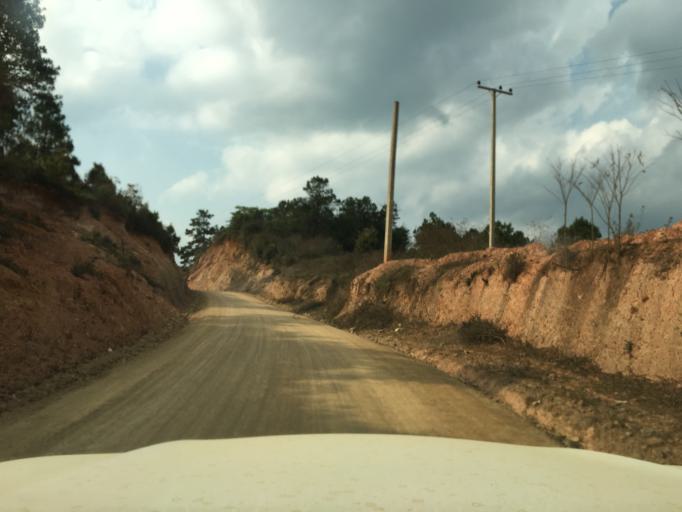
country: LA
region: Houaphan
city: Huameung
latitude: 20.2100
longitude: 103.8718
